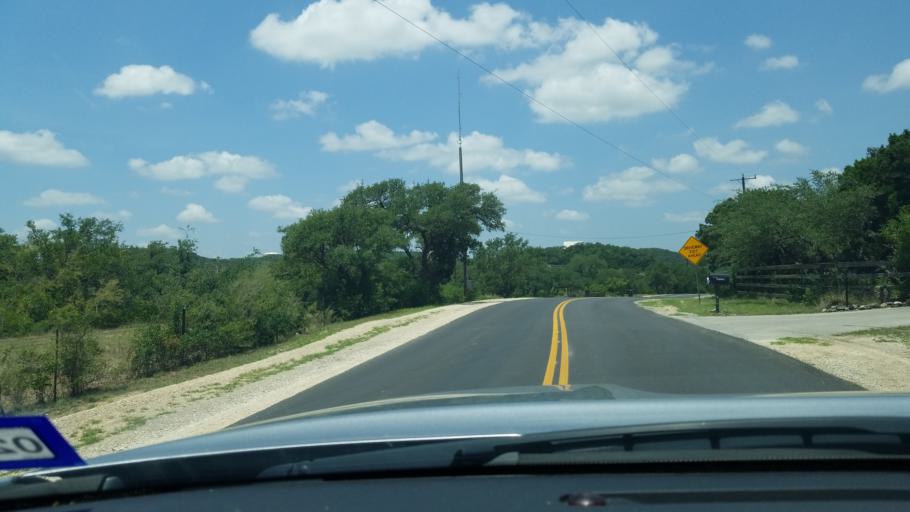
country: US
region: Texas
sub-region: Bexar County
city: Timberwood Park
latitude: 29.7026
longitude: -98.4553
